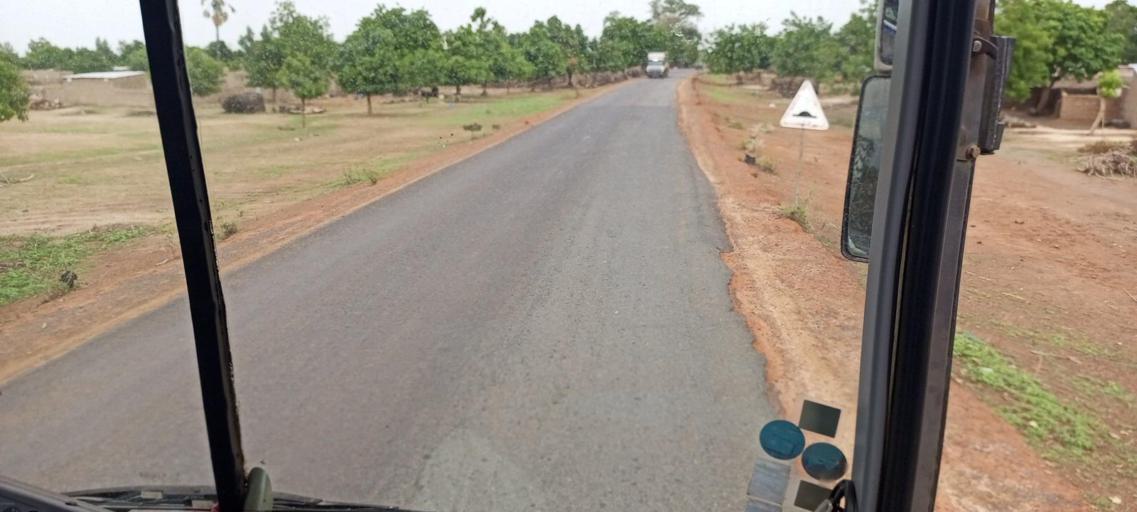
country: ML
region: Segou
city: Bla
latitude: 12.7374
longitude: -5.7270
